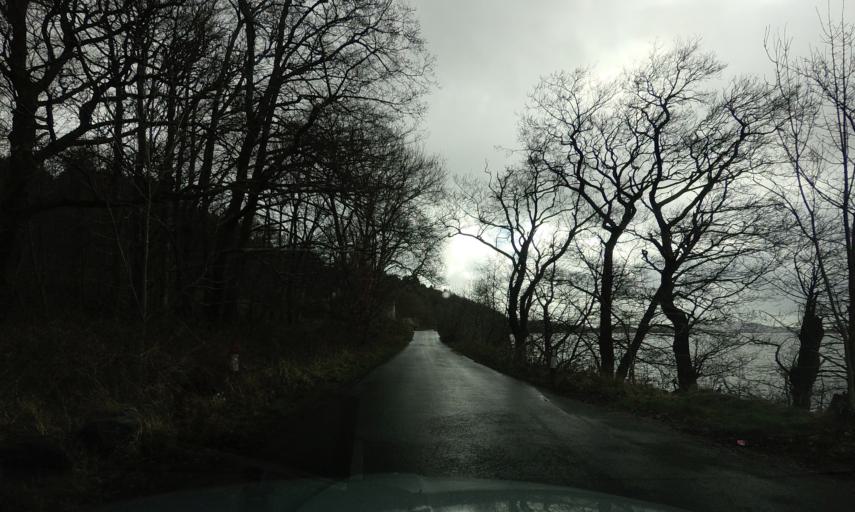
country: GB
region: Scotland
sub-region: West Dunbartonshire
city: Balloch
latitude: 56.1192
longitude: -4.5901
